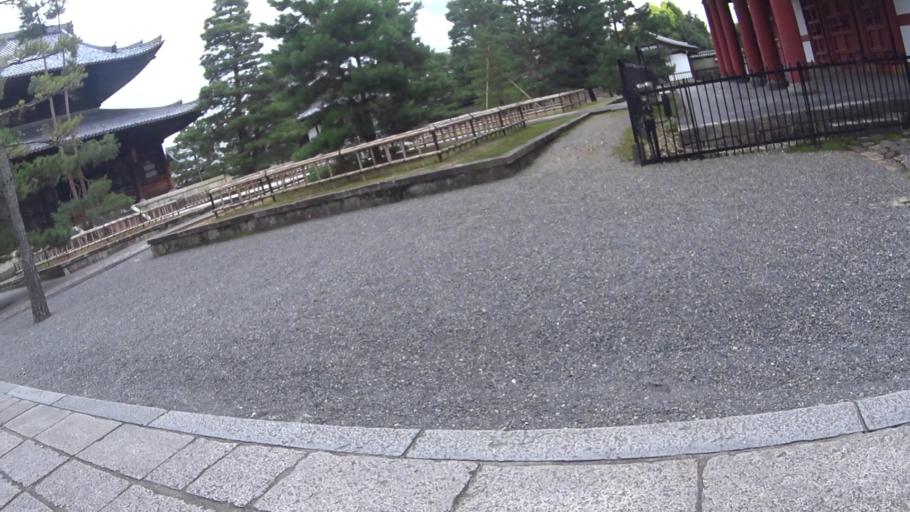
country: JP
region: Kyoto
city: Kyoto
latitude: 35.0217
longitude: 135.7198
